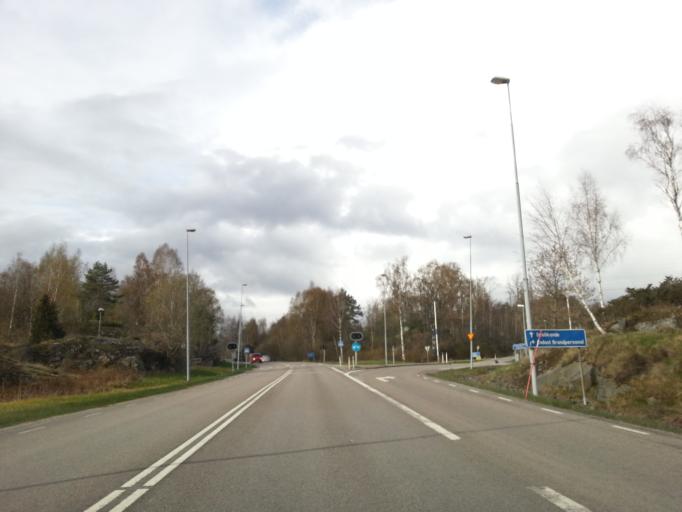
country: SE
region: Vaestra Goetaland
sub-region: Kungalvs Kommun
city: Kungalv
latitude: 57.8796
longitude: 11.9716
